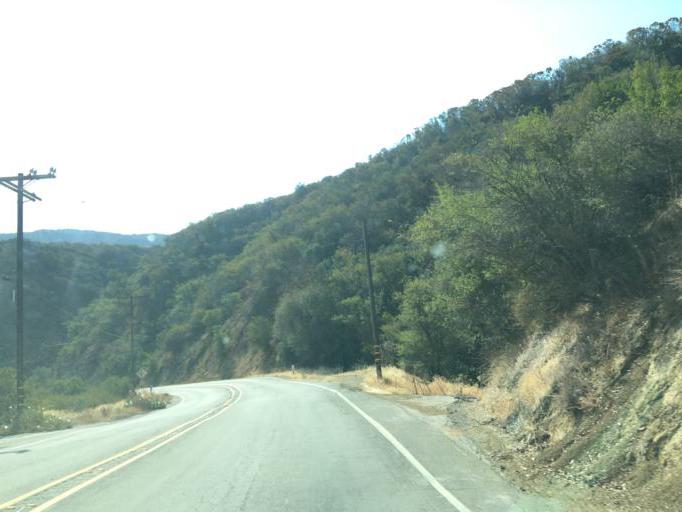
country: US
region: California
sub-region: Los Angeles County
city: Topanga
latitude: 34.0906
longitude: -118.6556
